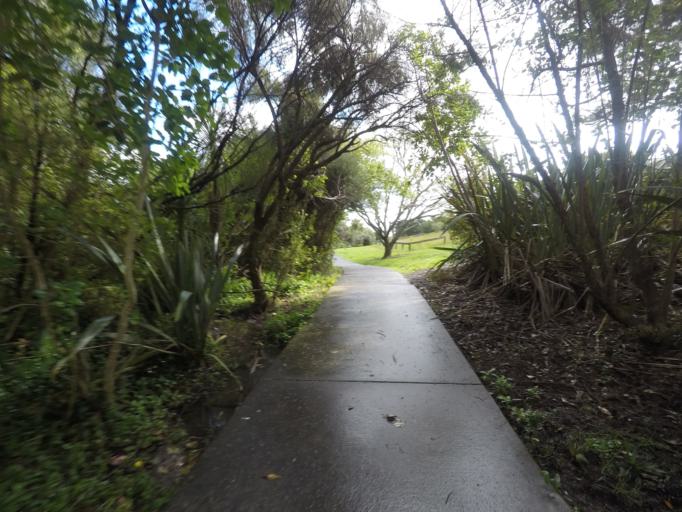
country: NZ
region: Auckland
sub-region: Auckland
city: Rosebank
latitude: -36.9026
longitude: 174.6998
